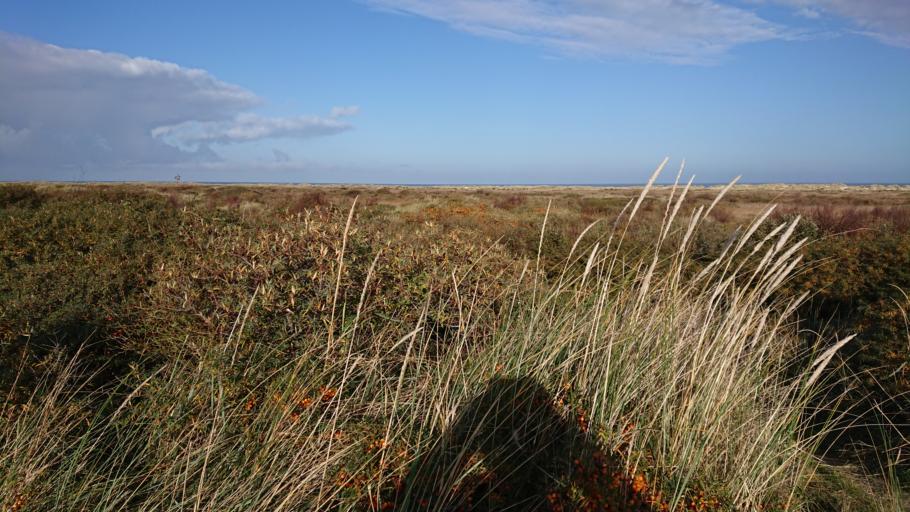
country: DK
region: North Denmark
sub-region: Frederikshavn Kommune
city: Skagen
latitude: 57.7454
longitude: 10.6329
